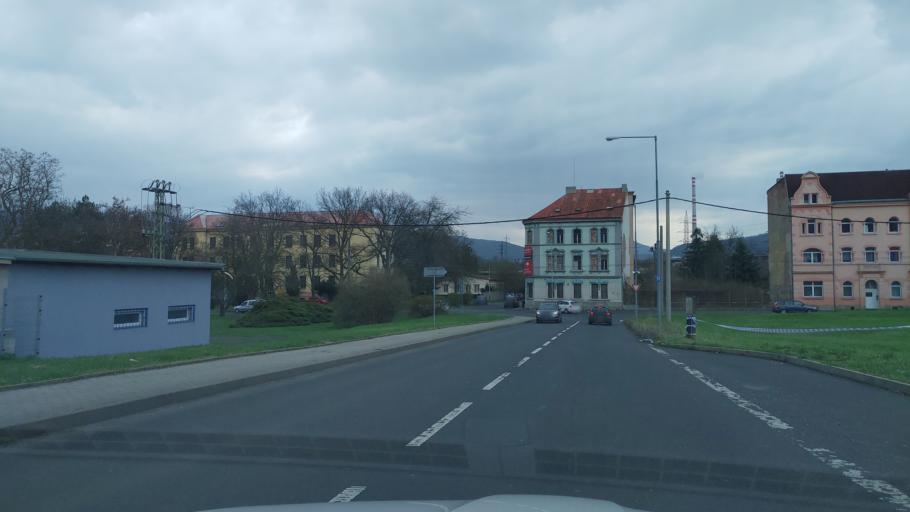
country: CZ
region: Ustecky
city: Trmice
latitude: 50.6582
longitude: 13.9941
